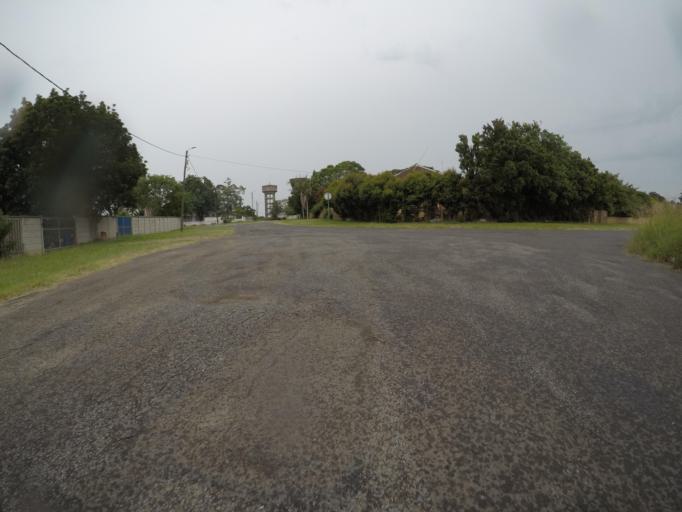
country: ZA
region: Eastern Cape
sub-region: Buffalo City Metropolitan Municipality
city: East London
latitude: -32.9689
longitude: 27.8300
